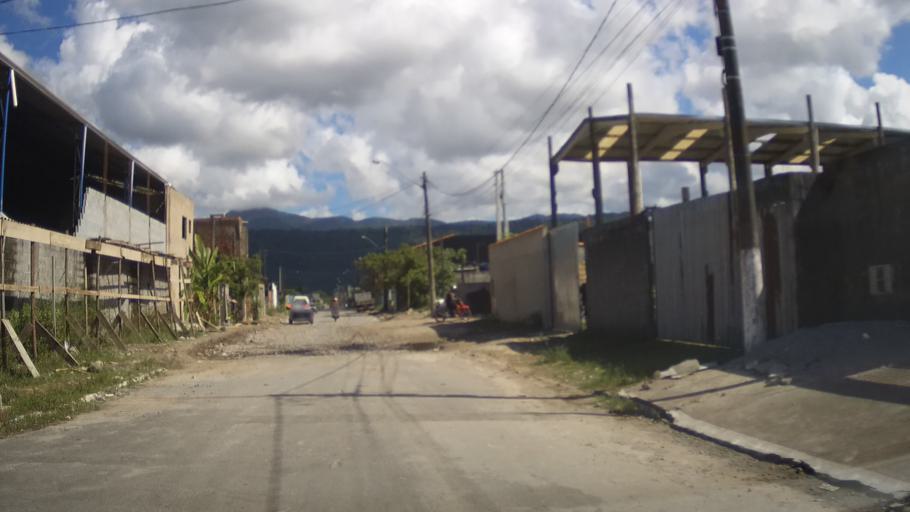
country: BR
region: Sao Paulo
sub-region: Praia Grande
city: Praia Grande
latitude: -24.0214
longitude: -46.5165
